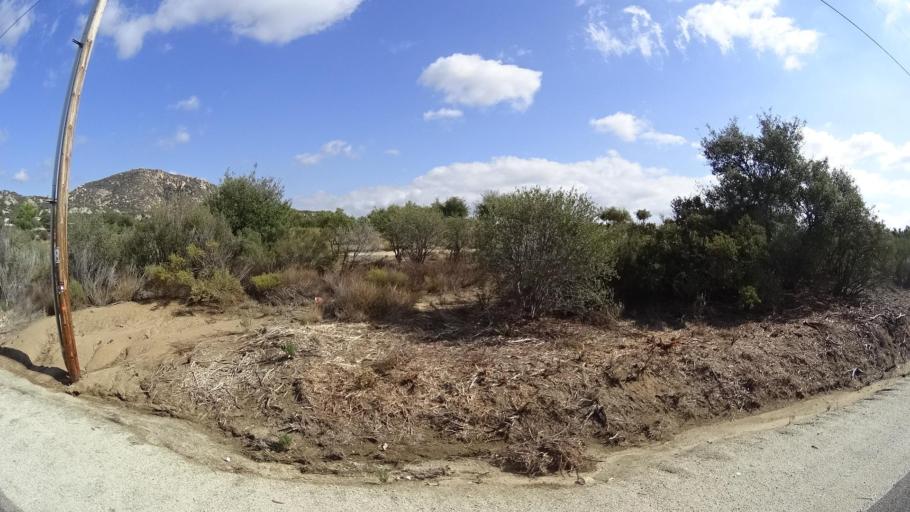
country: US
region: California
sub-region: San Diego County
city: Campo
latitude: 32.6855
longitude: -116.4962
